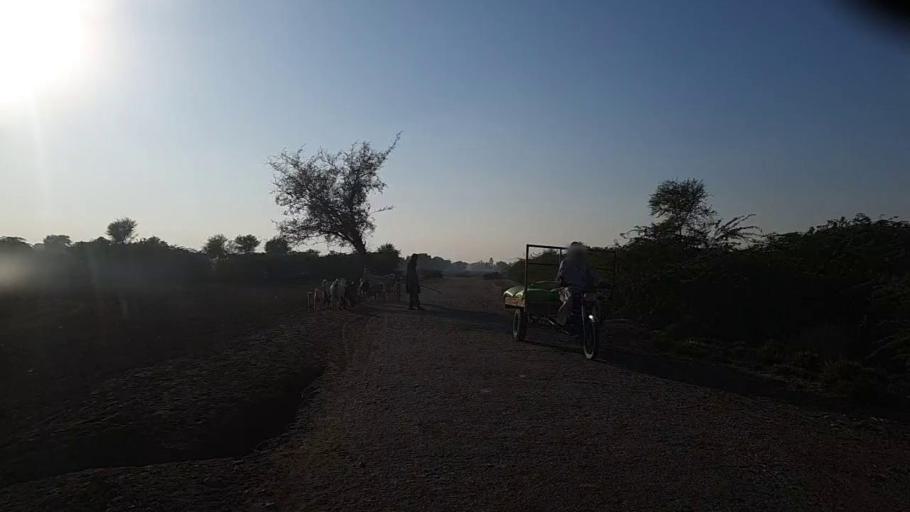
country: PK
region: Sindh
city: Pad Idan
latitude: 26.7345
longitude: 68.3432
